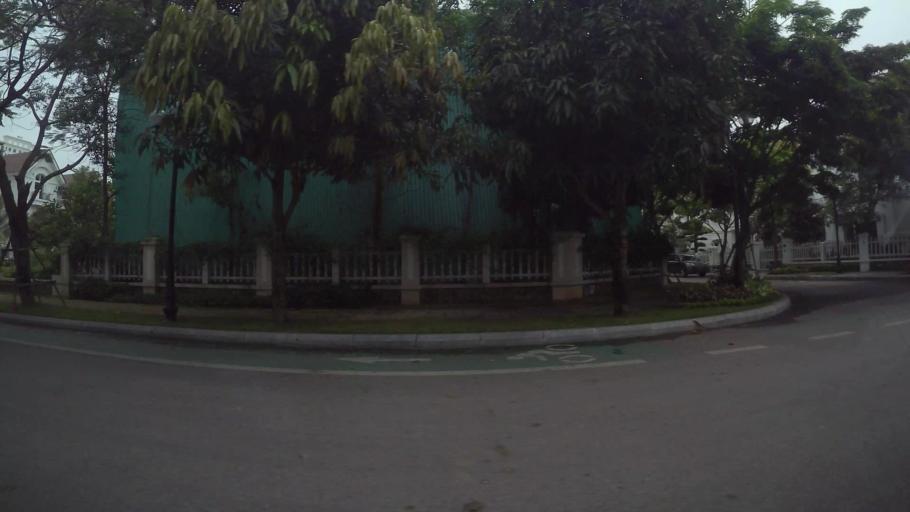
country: VN
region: Ha Noi
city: Trau Quy
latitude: 21.0541
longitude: 105.9135
